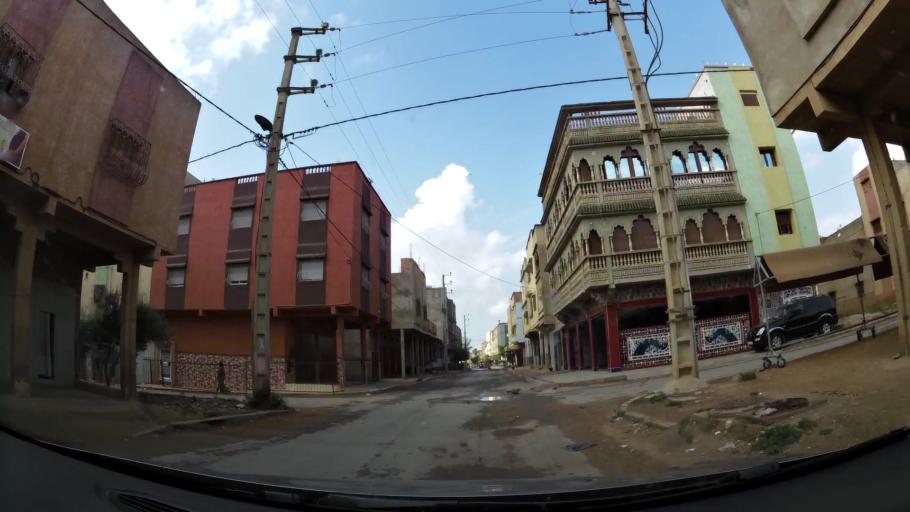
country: MA
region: Rabat-Sale-Zemmour-Zaer
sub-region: Khemisset
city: Tiflet
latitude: 33.8976
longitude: -6.3154
